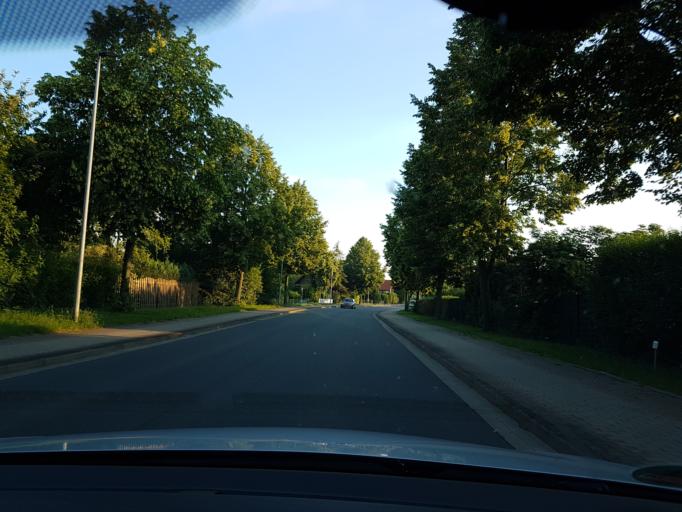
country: DE
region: Lower Saxony
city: Schoningen
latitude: 52.1561
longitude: 10.9649
